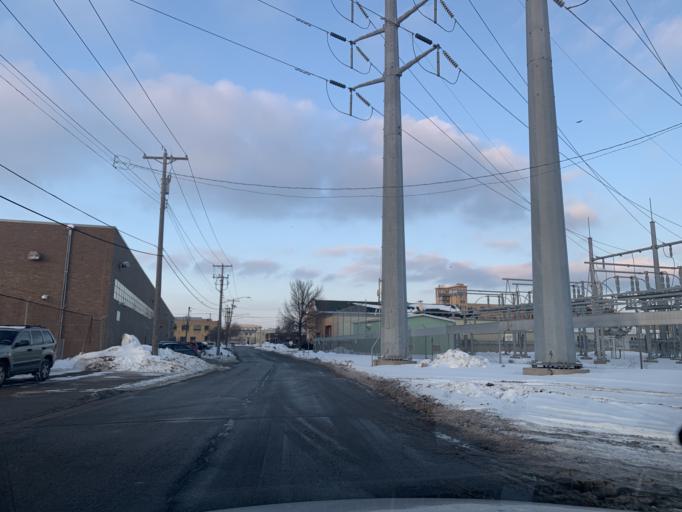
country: US
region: Minnesota
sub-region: Hennepin County
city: Minneapolis
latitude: 44.9773
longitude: -93.2917
